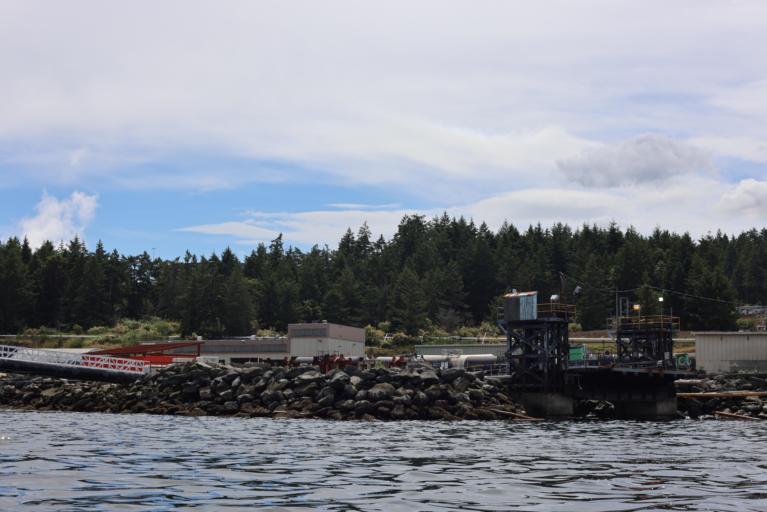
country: CA
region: British Columbia
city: Nanaimo
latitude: 49.1414
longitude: -123.8653
